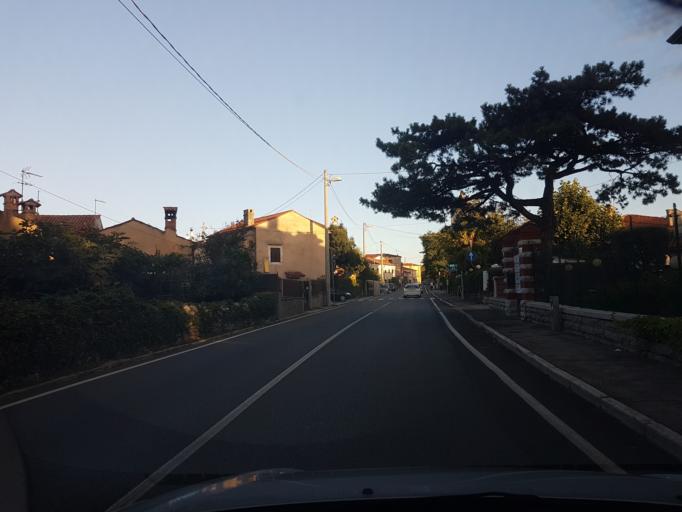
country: IT
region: Friuli Venezia Giulia
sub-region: Provincia di Trieste
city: Villa Opicina
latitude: 45.6914
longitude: 13.7865
